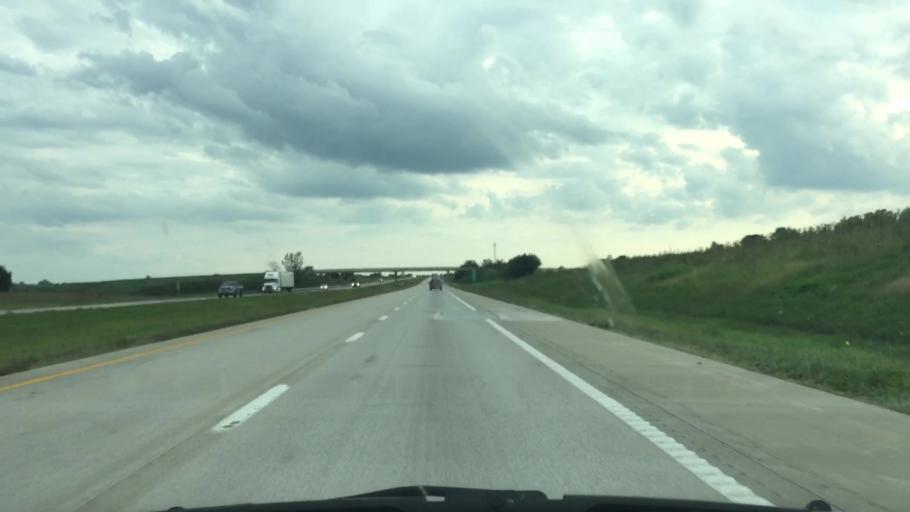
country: US
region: Missouri
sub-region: Clinton County
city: Lathrop
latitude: 39.5891
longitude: -94.2570
